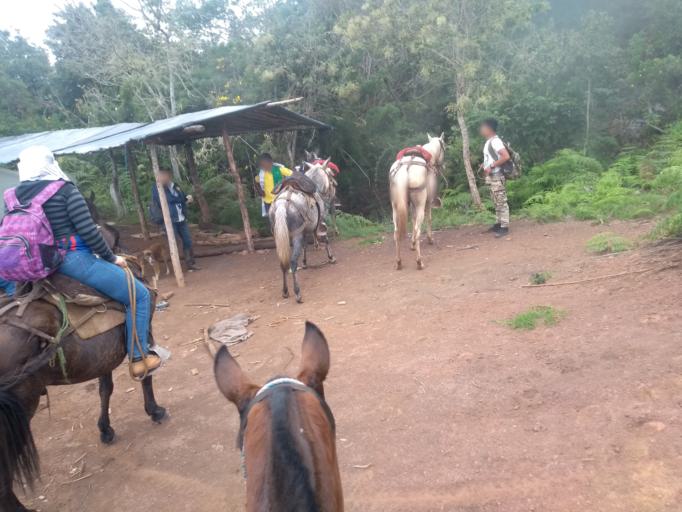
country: CO
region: Cesar
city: San Diego
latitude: 10.1788
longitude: -73.0430
